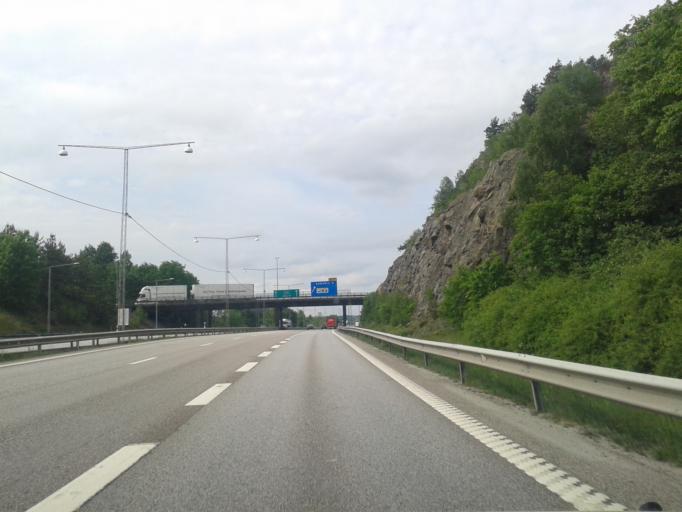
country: SE
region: Vaestra Goetaland
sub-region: Kungalvs Kommun
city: Kungalv
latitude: 57.8833
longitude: 11.9474
